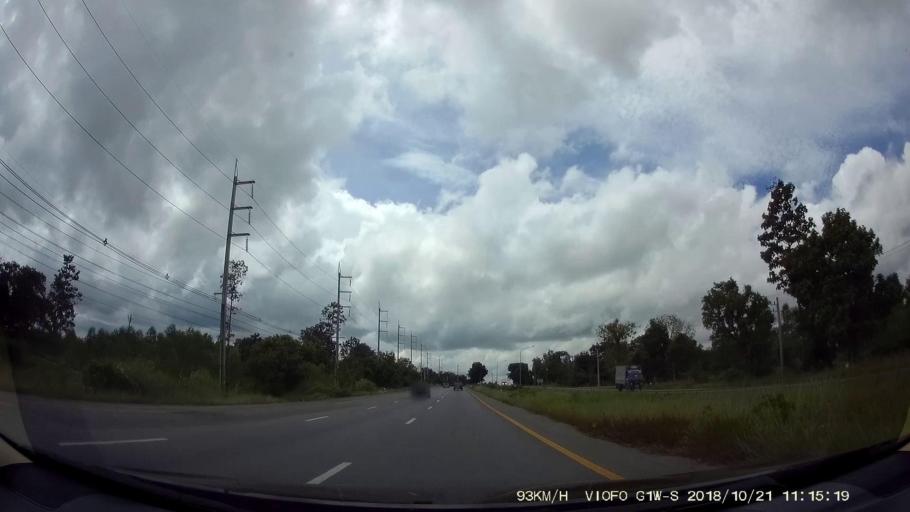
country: TH
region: Chaiyaphum
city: Chaiyaphum
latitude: 15.8936
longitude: 102.1169
